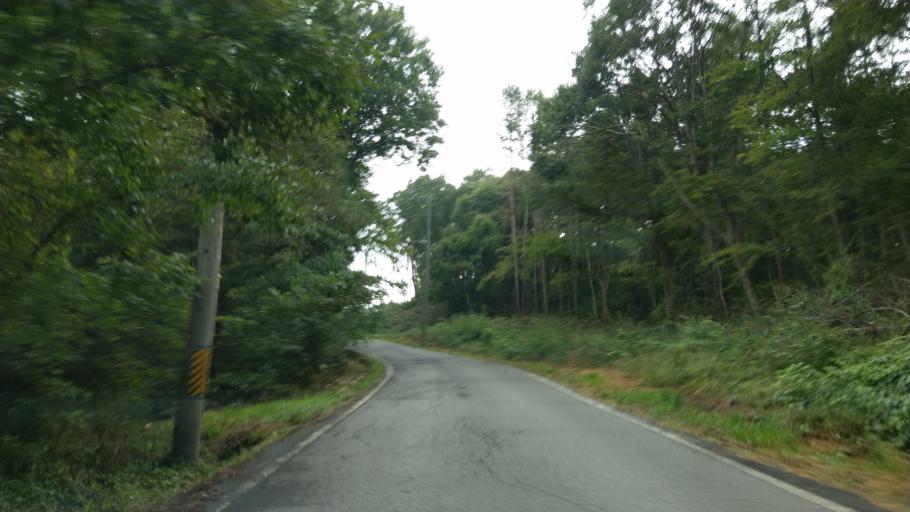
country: JP
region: Nagano
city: Komoro
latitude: 36.3069
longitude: 138.3912
